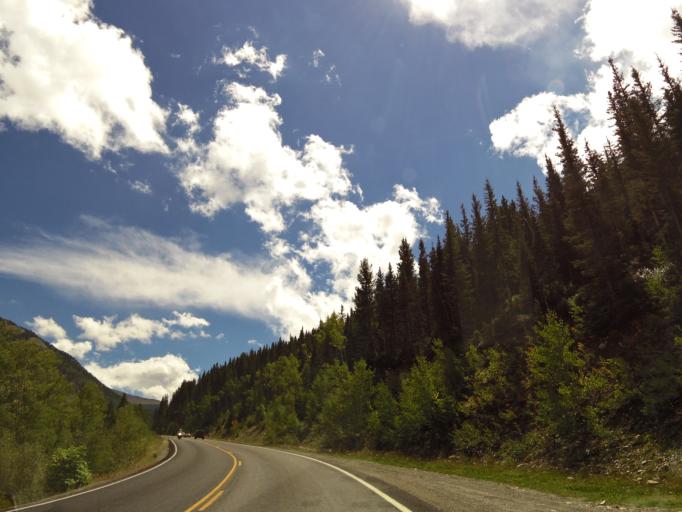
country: US
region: Colorado
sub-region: San Juan County
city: Silverton
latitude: 37.8022
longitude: -107.6775
